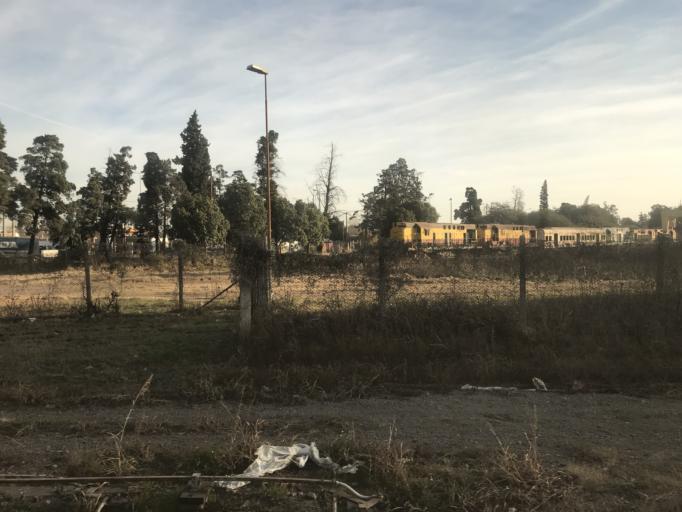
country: AR
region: Cordoba
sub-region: Departamento de Capital
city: Cordoba
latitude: -31.4596
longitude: -64.1088
